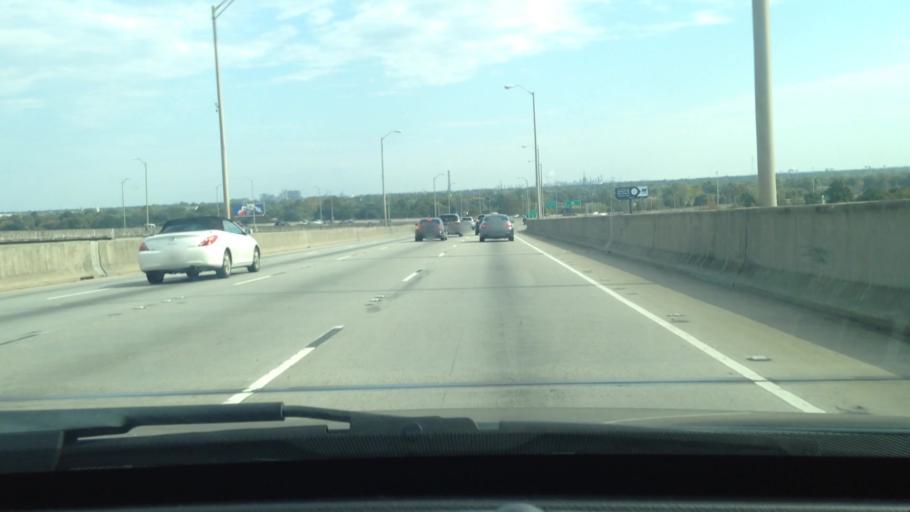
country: US
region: Louisiana
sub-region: Jefferson Parish
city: Gretna
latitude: 29.9378
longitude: -90.0456
